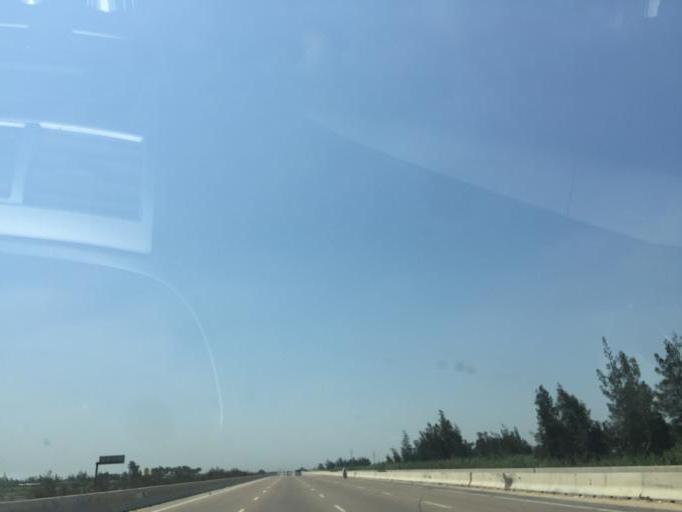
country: EG
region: Al Buhayrah
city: Abu al Matamir
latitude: 30.7449
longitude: 30.0027
